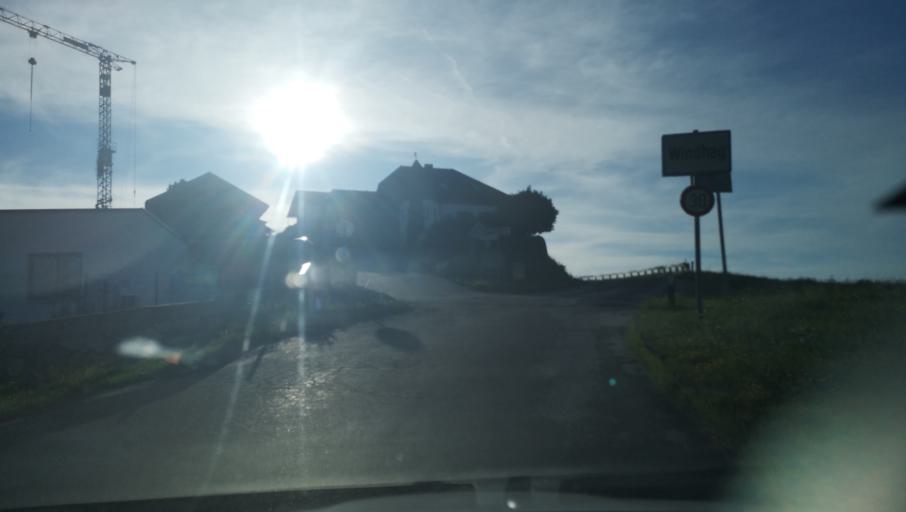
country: AT
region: Lower Austria
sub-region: Waidhofen an der Ybbs Stadt
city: Waidhofen an der Ybbs
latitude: 47.9796
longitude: 14.8051
